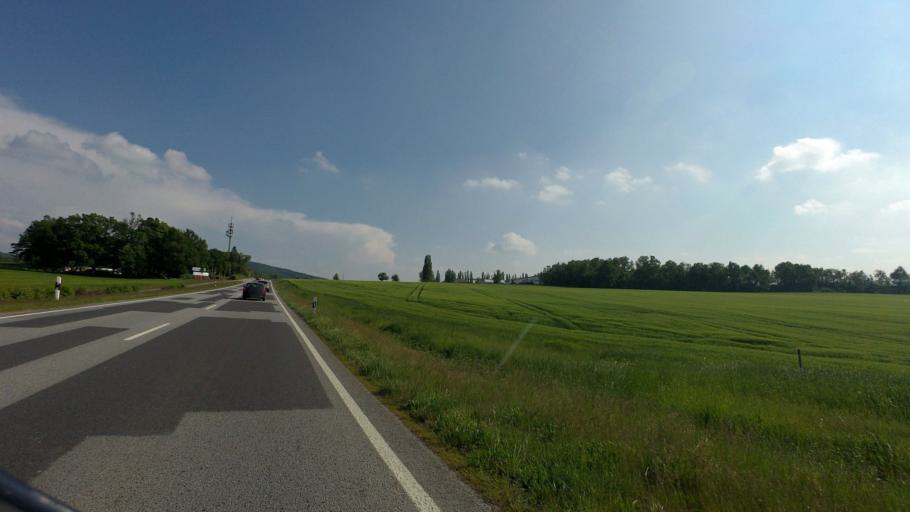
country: DE
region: Saxony
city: Bautzen
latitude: 51.1525
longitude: 14.4348
